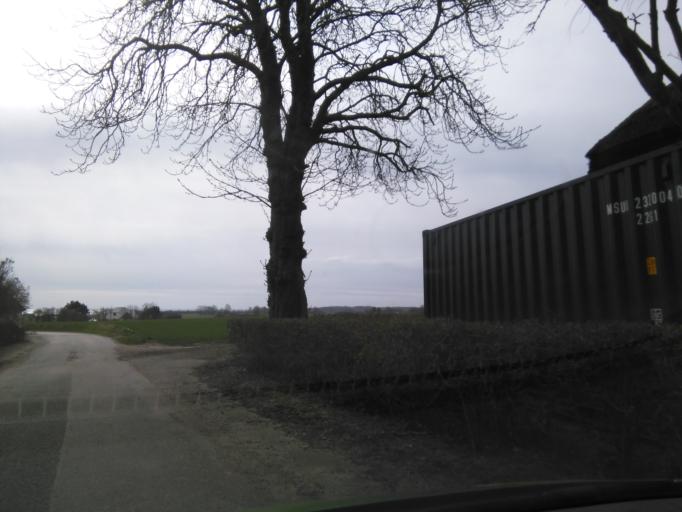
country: DK
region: Central Jutland
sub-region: Odder Kommune
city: Odder
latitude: 55.9483
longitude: 10.2539
